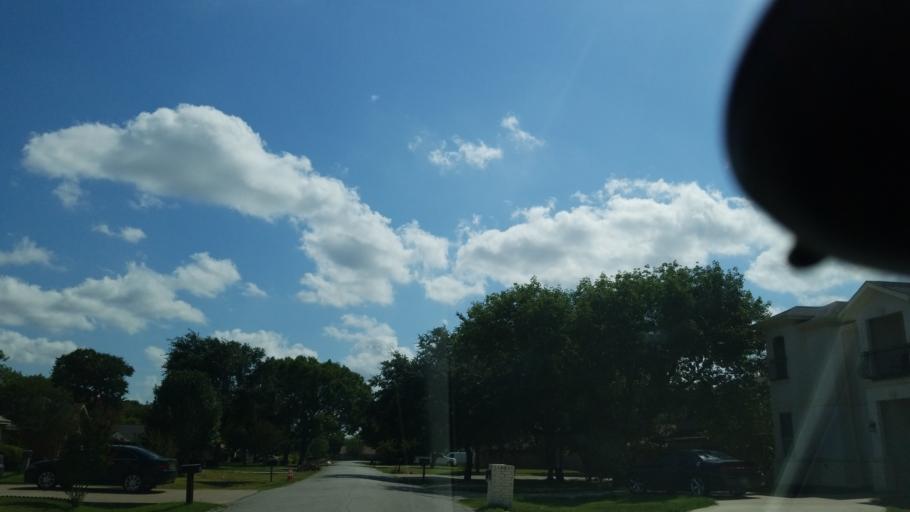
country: US
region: Texas
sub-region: Dallas County
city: Grand Prairie
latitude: 32.7114
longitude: -96.9986
